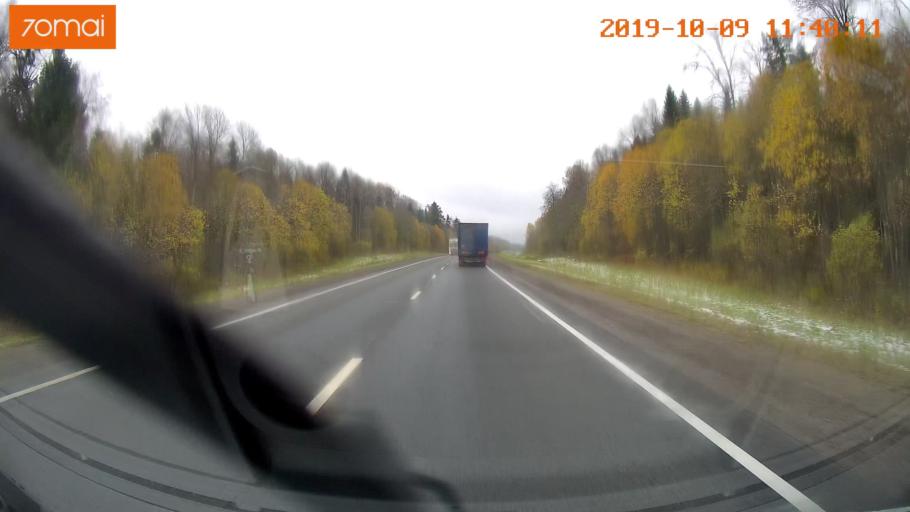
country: RU
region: Vologda
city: Gryazovets
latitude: 58.9461
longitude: 40.1730
